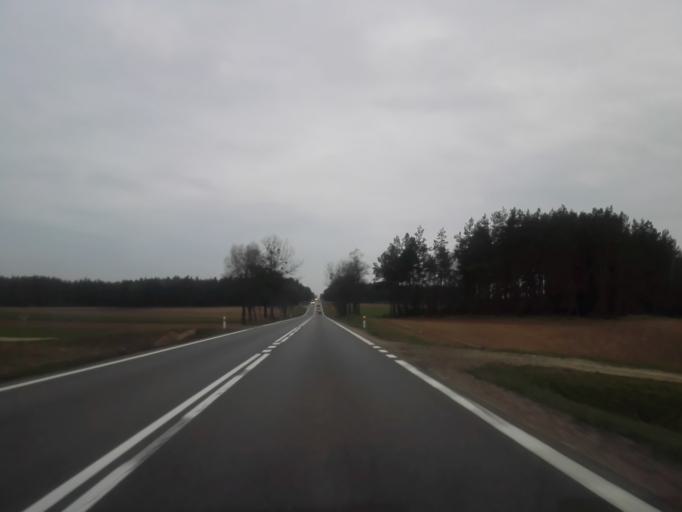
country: PL
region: Podlasie
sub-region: Powiat kolnenski
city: Stawiski
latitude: 53.4506
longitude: 22.1868
